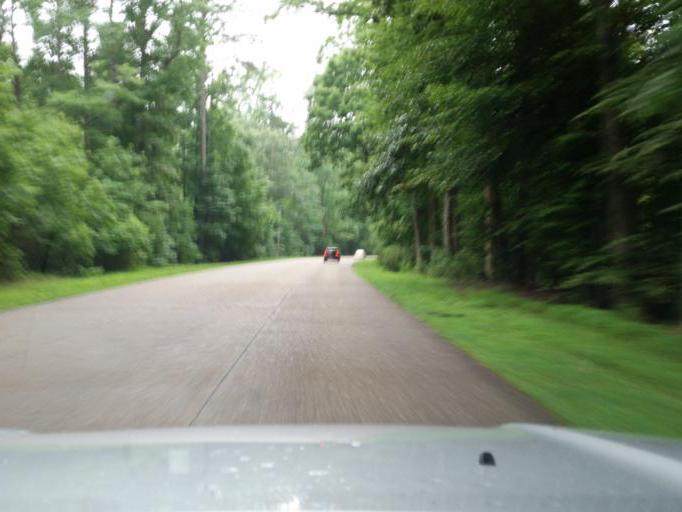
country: US
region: Virginia
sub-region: City of Williamsburg
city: Williamsburg
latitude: 37.2823
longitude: -76.6489
